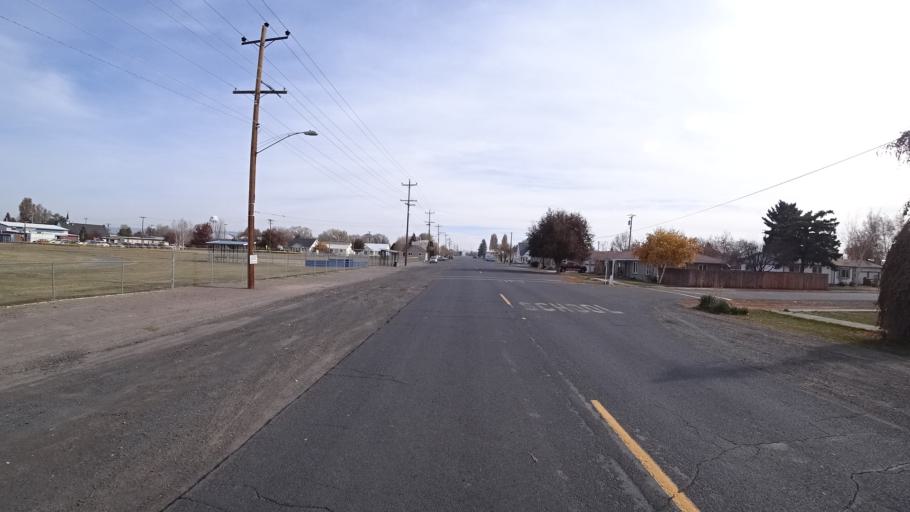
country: US
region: California
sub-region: Siskiyou County
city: Tulelake
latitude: 41.9537
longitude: -121.4795
